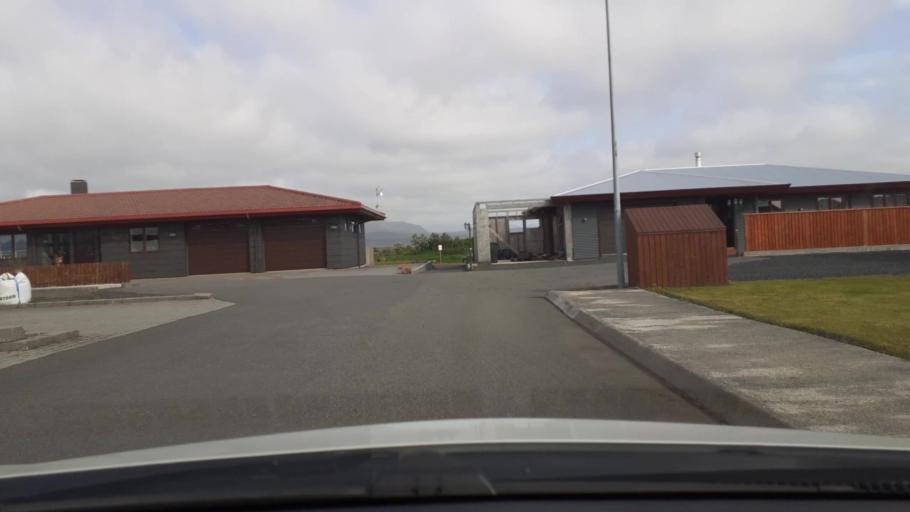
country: IS
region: South
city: THorlakshoefn
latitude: 63.8577
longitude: -21.3968
